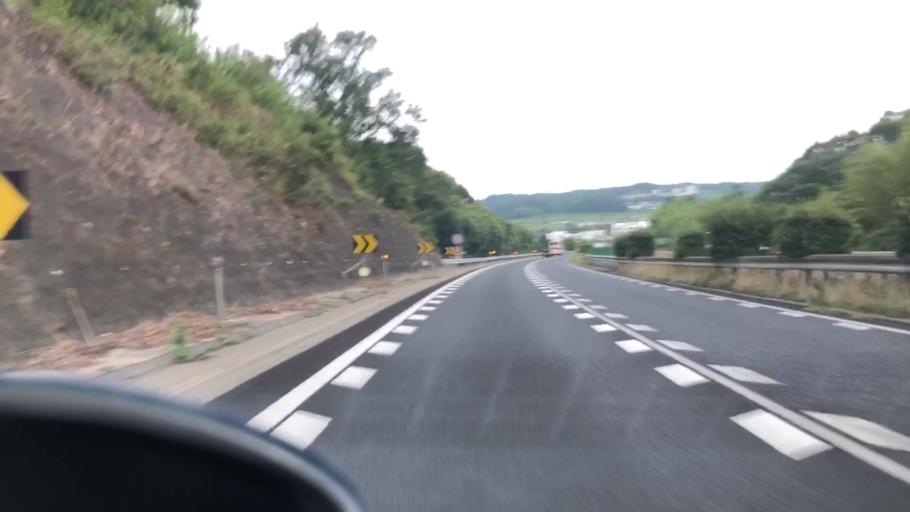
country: JP
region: Hyogo
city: Yashiro
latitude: 34.9104
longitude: 135.0563
